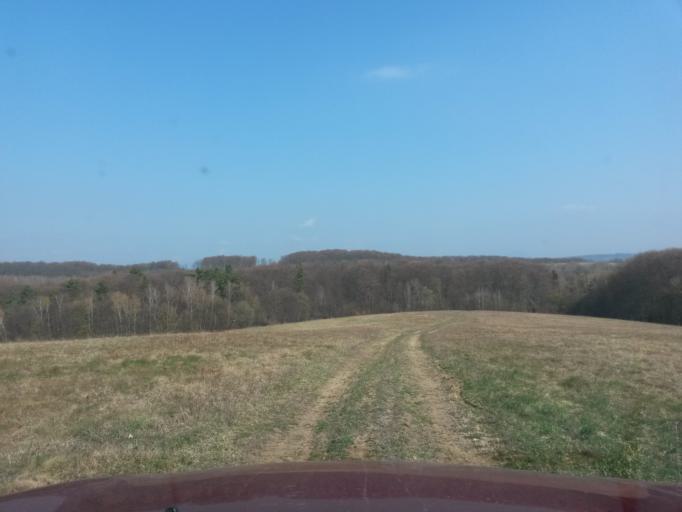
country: SK
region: Presovsky
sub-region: Okres Presov
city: Presov
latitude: 48.9325
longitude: 21.1441
